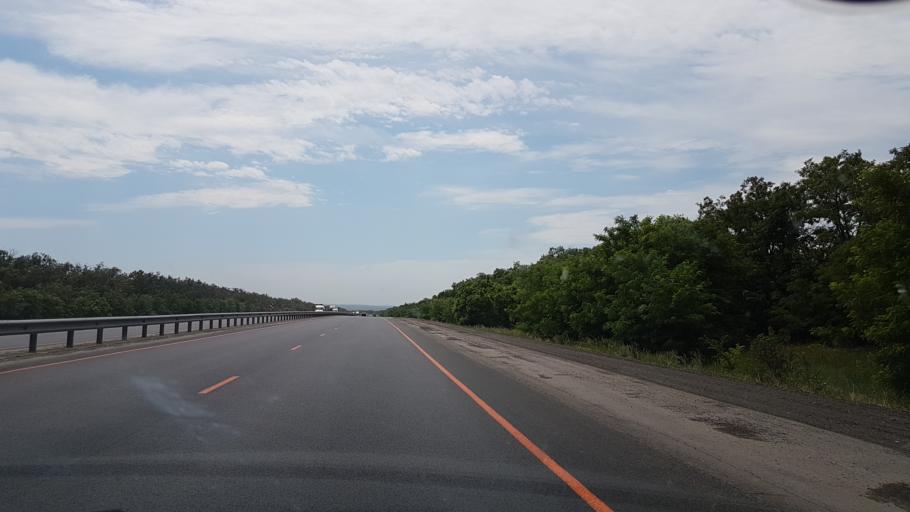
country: RU
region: Rostov
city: Zverevo
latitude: 47.9961
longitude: 40.2287
